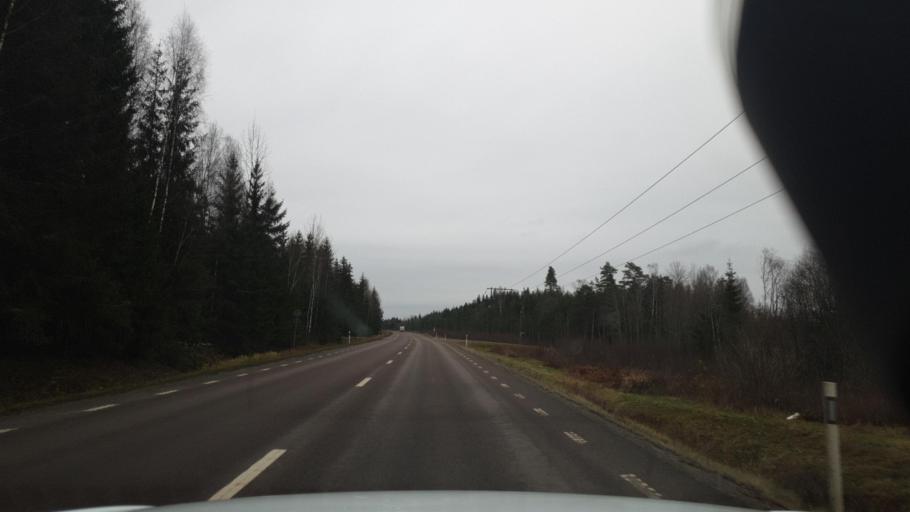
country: SE
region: Vaermland
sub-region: Karlstads Kommun
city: Edsvalla
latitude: 59.4298
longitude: 13.1979
